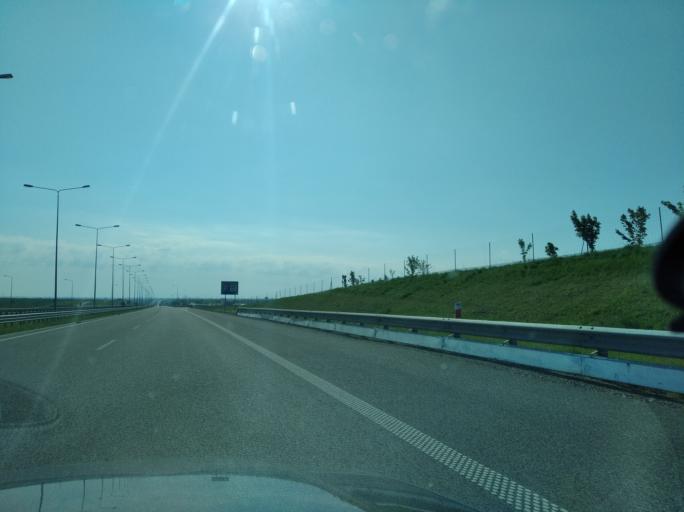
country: PL
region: Subcarpathian Voivodeship
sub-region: Powiat jaroslawski
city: Ostrow
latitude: 49.9170
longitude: 22.7543
